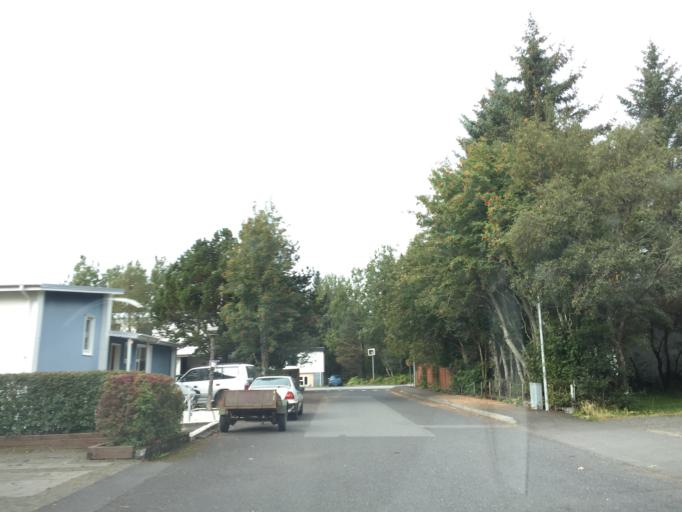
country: IS
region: South
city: Selfoss
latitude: 63.9352
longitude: -20.9916
